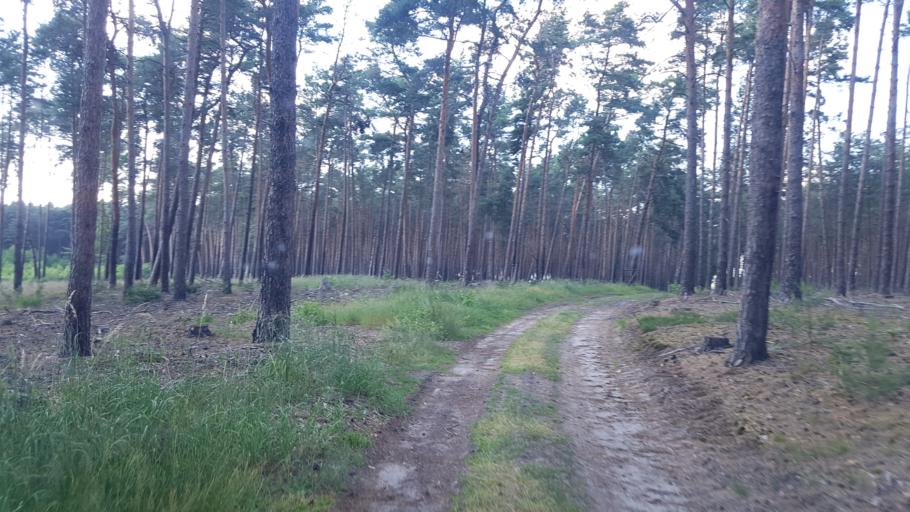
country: DE
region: Brandenburg
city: Trobitz
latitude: 51.6429
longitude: 13.4151
